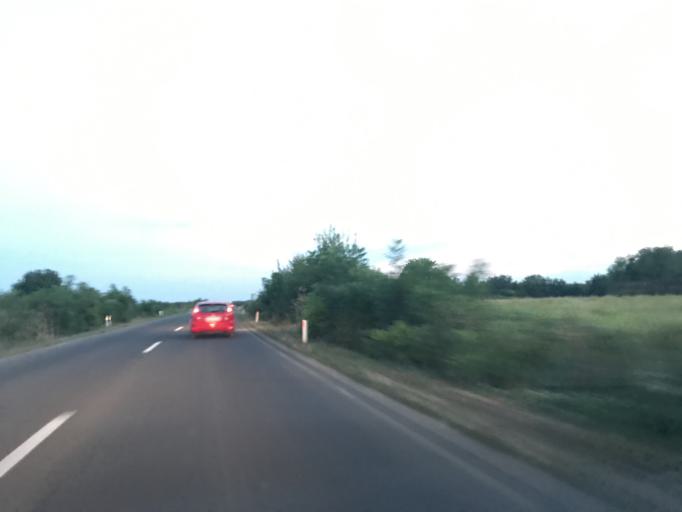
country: RS
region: Central Serbia
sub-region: Branicevski Okrug
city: Pozarevac
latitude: 44.6176
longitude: 21.1460
